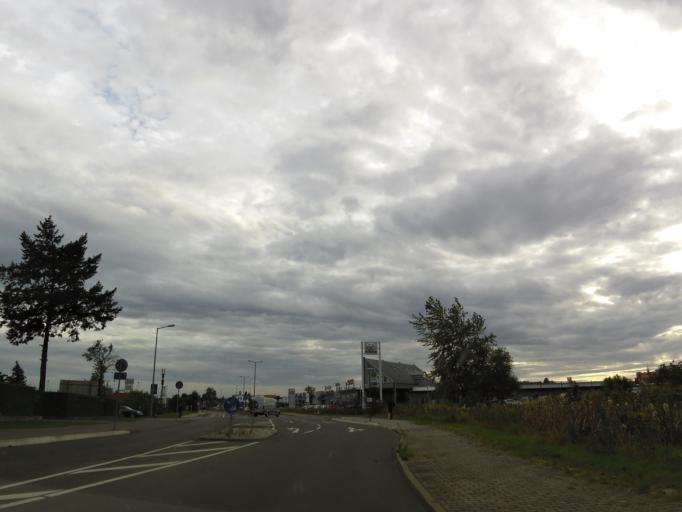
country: DE
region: Saxony
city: Markranstadt
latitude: 51.3485
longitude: 12.2630
